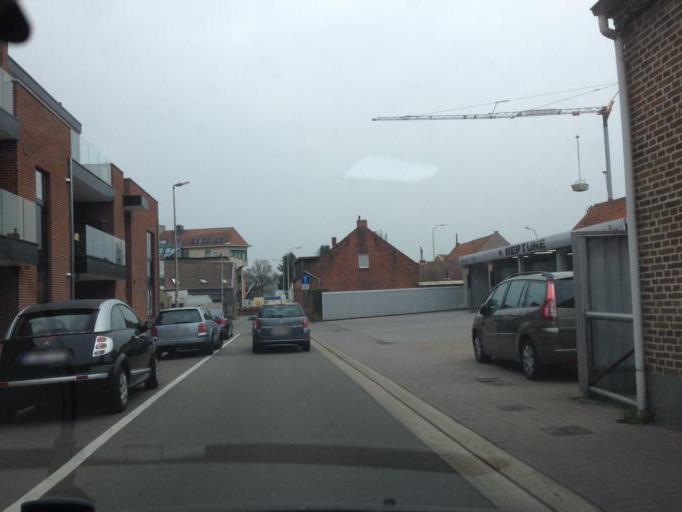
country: BE
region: Flanders
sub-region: Provincie Limburg
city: Bree
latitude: 51.1389
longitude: 5.5942
